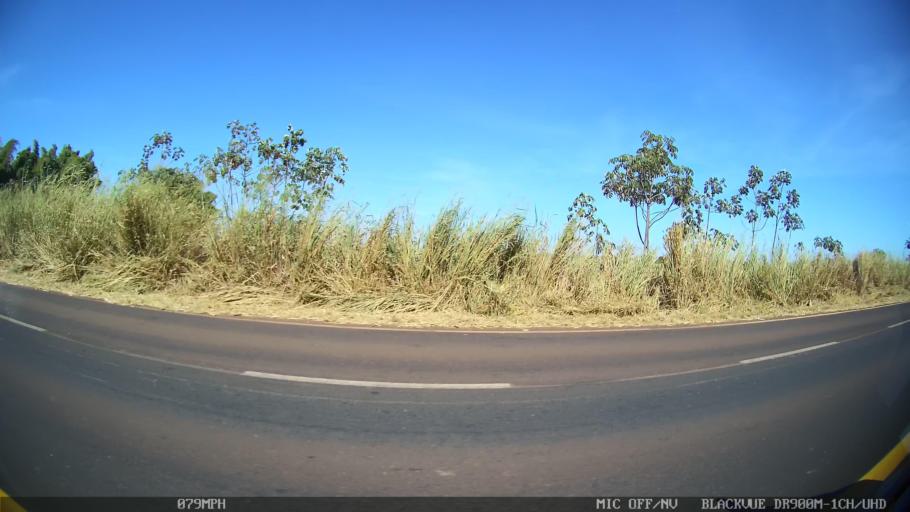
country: BR
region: Sao Paulo
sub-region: Barretos
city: Barretos
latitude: -20.4671
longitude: -48.4784
